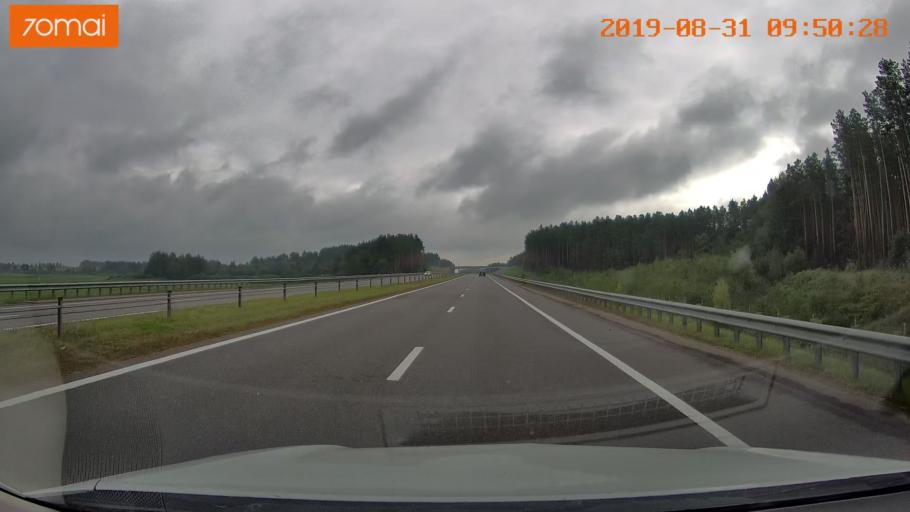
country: BY
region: Mogilev
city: Byalynichy
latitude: 53.9650
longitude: 29.7211
